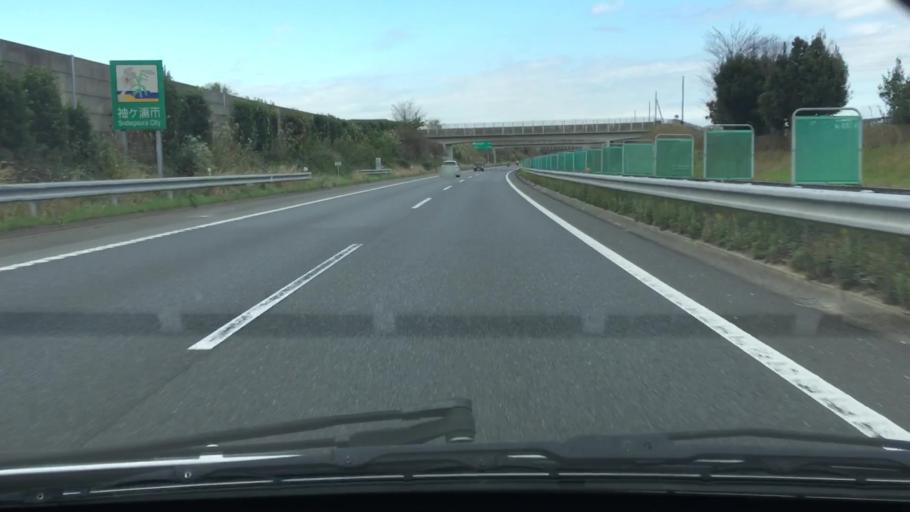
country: JP
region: Chiba
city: Ichihara
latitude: 35.4250
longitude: 140.0339
